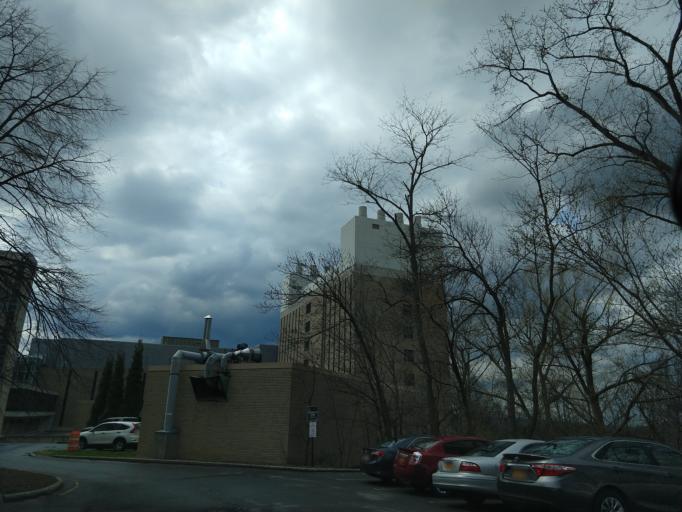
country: US
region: New York
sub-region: Tompkins County
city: East Ithaca
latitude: 42.4504
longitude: -76.4799
